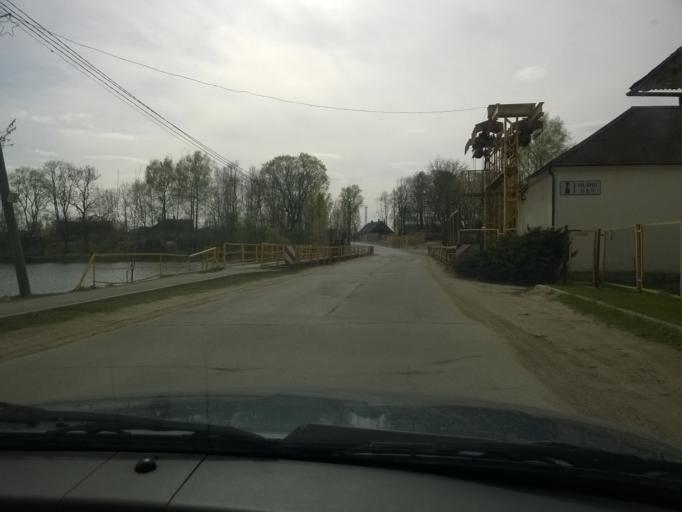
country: LV
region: Vilanu
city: Vilani
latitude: 56.5410
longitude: 26.9261
